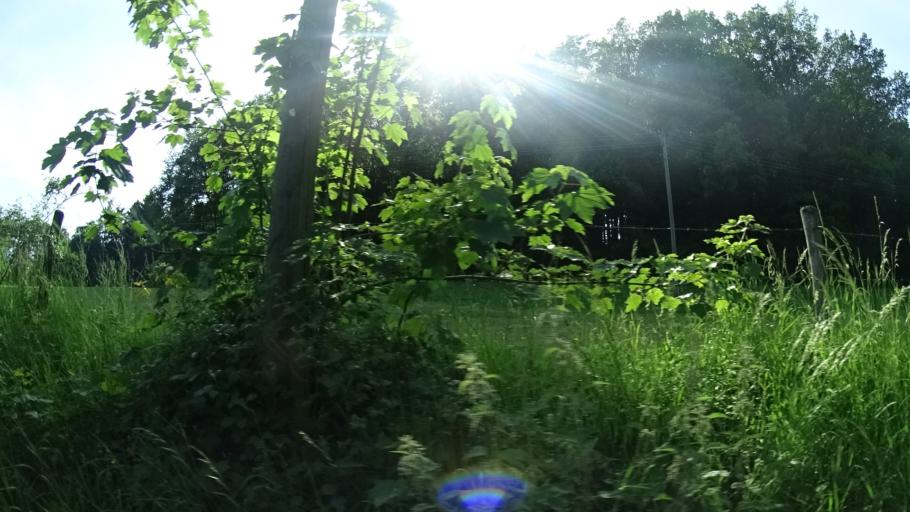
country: DE
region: Hesse
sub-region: Regierungsbezirk Darmstadt
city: Wald-Michelbach
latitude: 49.6100
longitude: 8.8240
